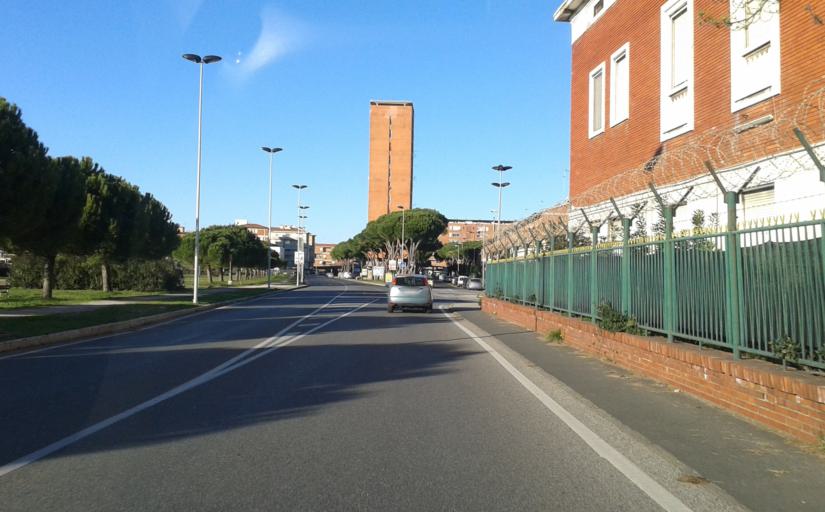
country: IT
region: Tuscany
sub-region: Provincia di Livorno
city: Livorno
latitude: 43.5206
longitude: 10.3244
